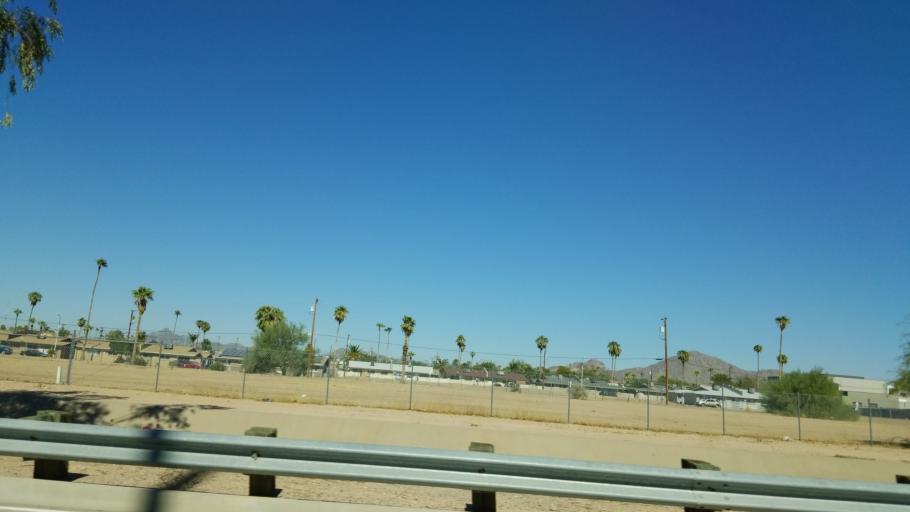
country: US
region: Arizona
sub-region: Maricopa County
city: Tempe Junction
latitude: 33.4594
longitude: -111.9926
